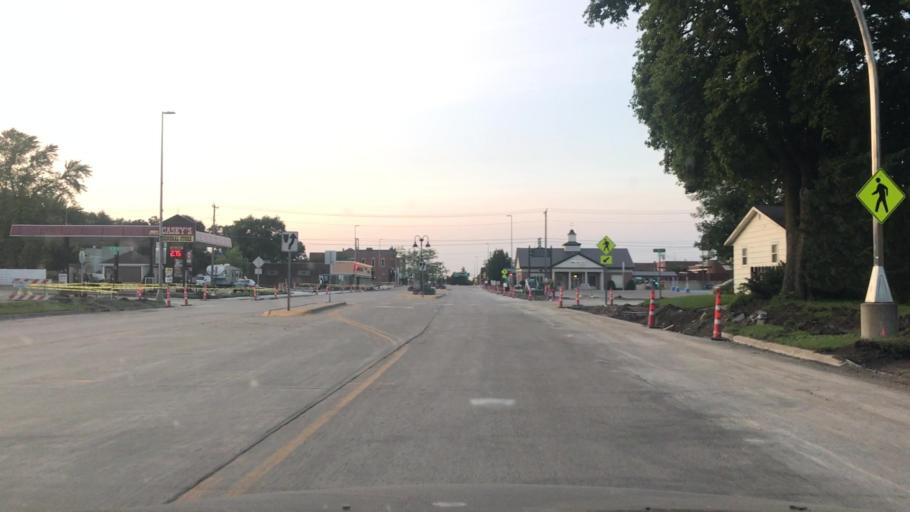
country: US
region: Minnesota
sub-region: Redwood County
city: Redwood Falls
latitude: 44.5373
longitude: -95.1194
